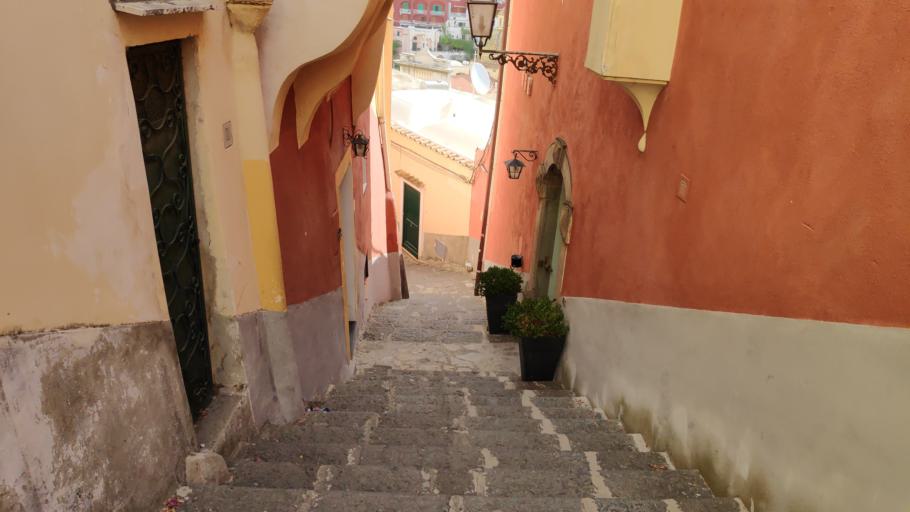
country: IT
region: Campania
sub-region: Provincia di Salerno
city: Positano
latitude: 40.6276
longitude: 14.4856
